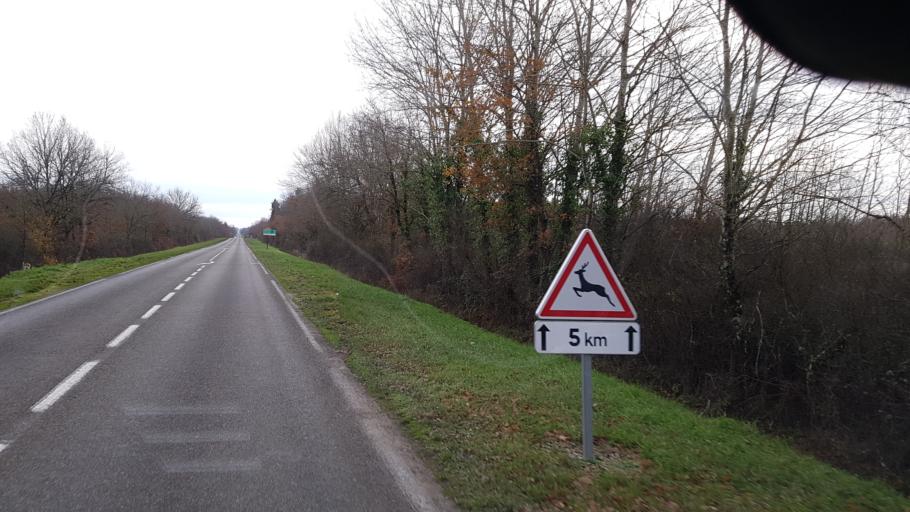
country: FR
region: Centre
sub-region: Departement du Loiret
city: La Ferte-Saint-Aubin
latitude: 47.7034
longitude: 1.9463
